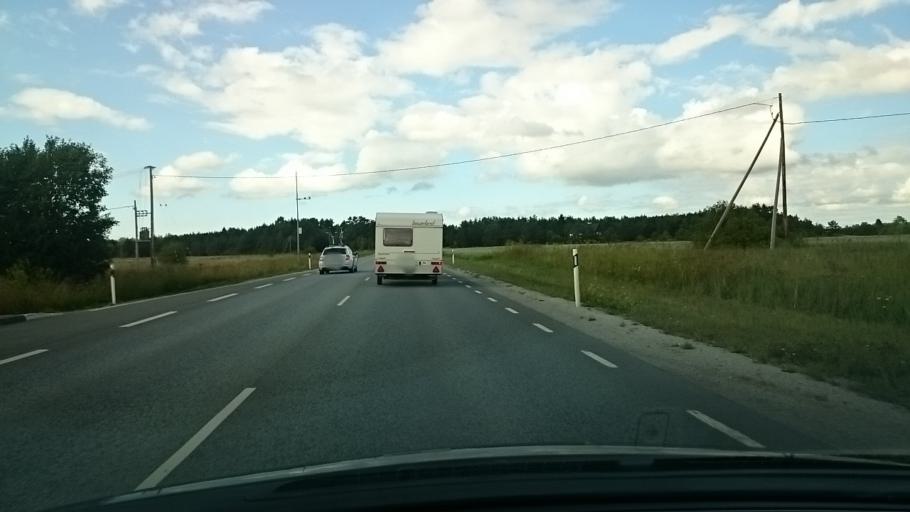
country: EE
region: Harju
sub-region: Keila linn
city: Keila
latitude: 59.2646
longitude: 24.2916
